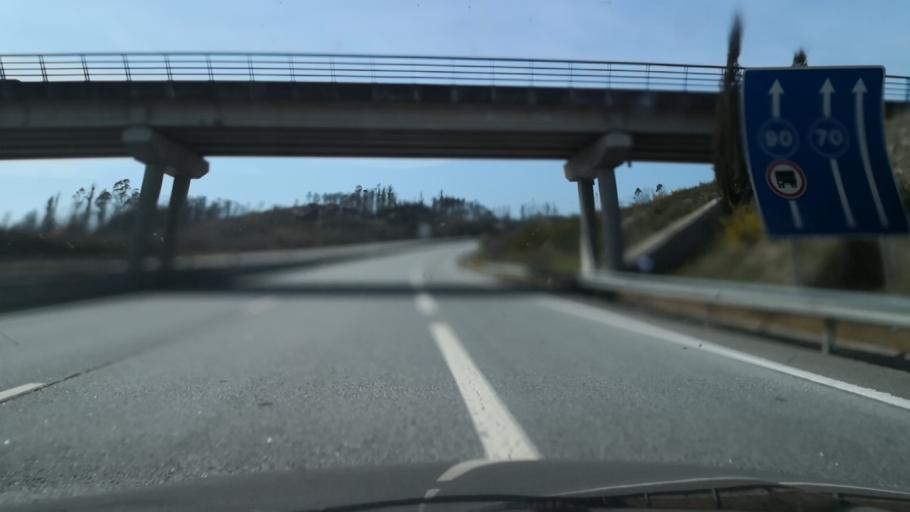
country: PT
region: Viseu
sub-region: Oliveira de Frades
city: Oliveira de Frades
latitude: 40.6852
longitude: -8.2214
